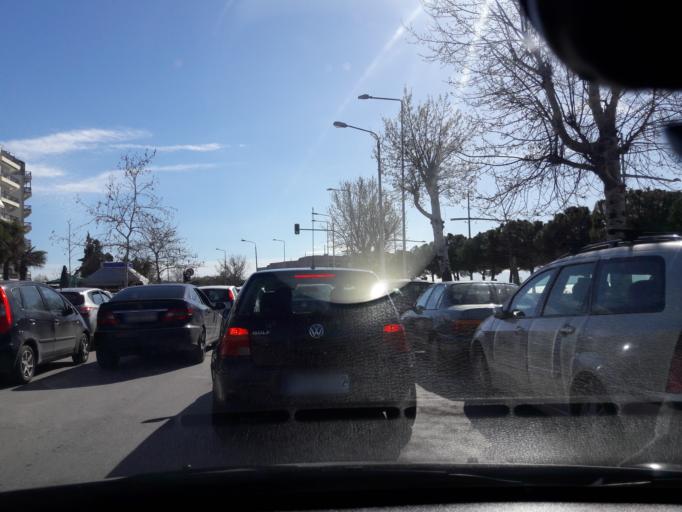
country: GR
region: Central Macedonia
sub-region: Nomos Thessalonikis
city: Kalamaria
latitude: 40.6015
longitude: 22.9497
